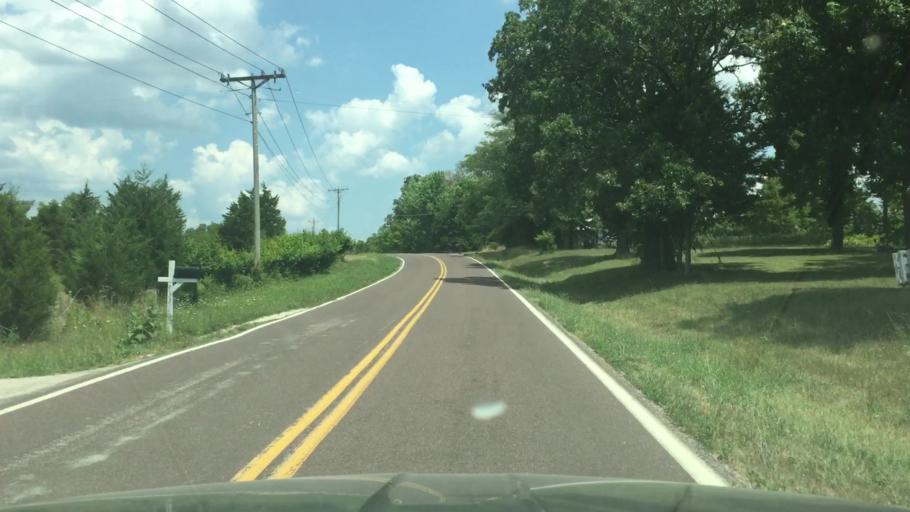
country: US
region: Missouri
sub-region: Miller County
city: Tuscumbia
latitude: 38.1060
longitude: -92.4732
